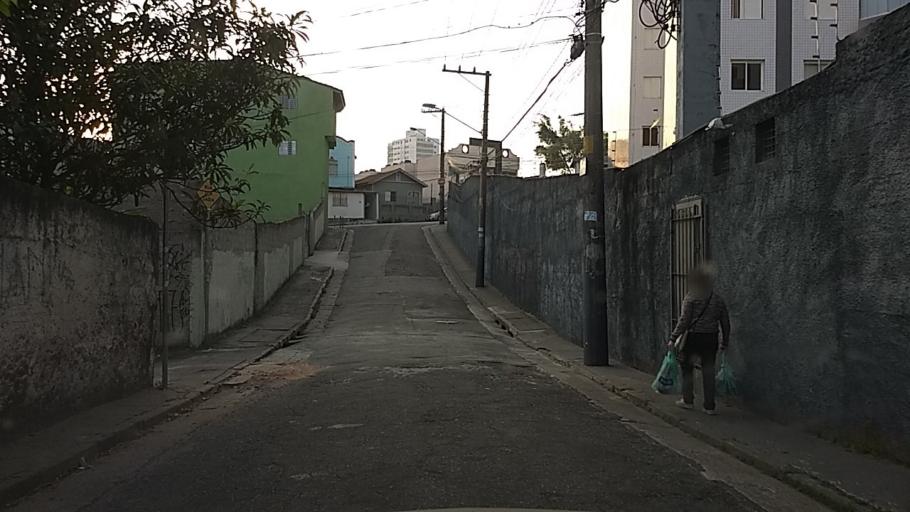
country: BR
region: Sao Paulo
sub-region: Sao Paulo
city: Sao Paulo
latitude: -23.5036
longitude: -46.5944
